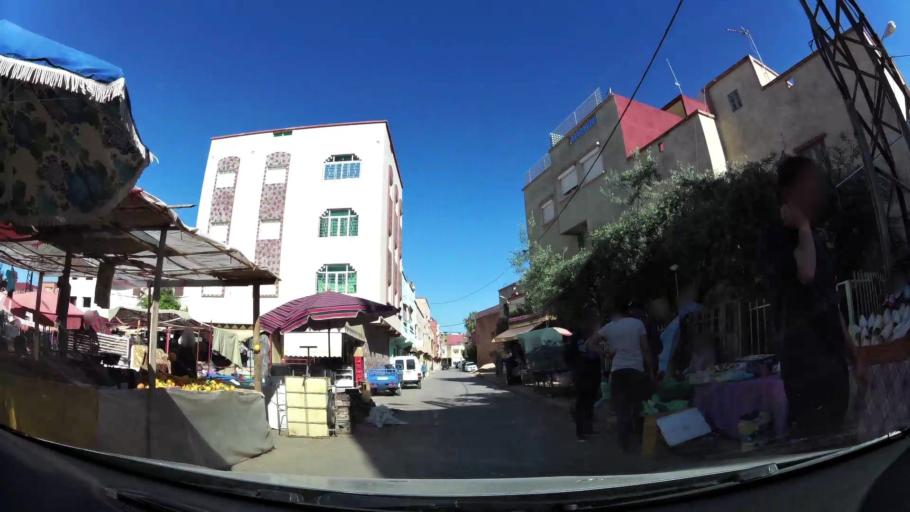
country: MA
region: Meknes-Tafilalet
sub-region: Meknes
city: Meknes
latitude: 33.8935
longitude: -5.5026
